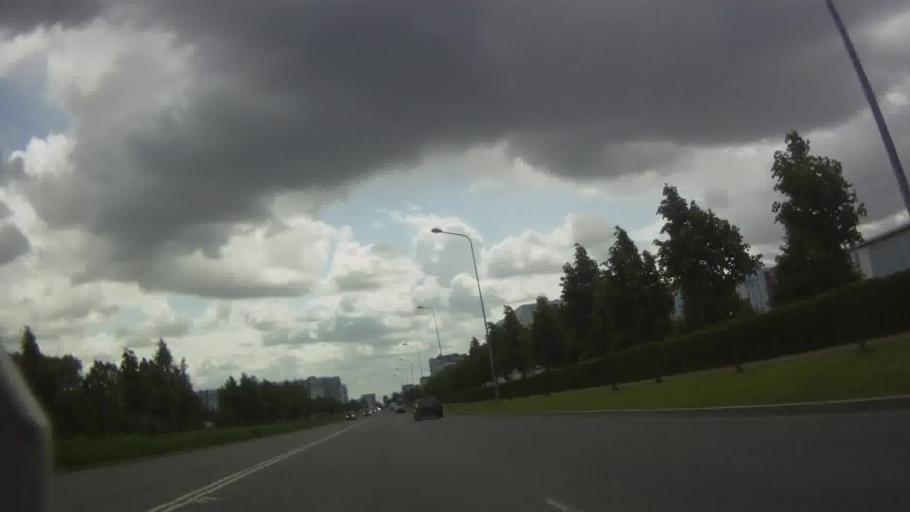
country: LV
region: Stopini
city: Ulbroka
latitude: 56.9494
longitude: 24.2195
